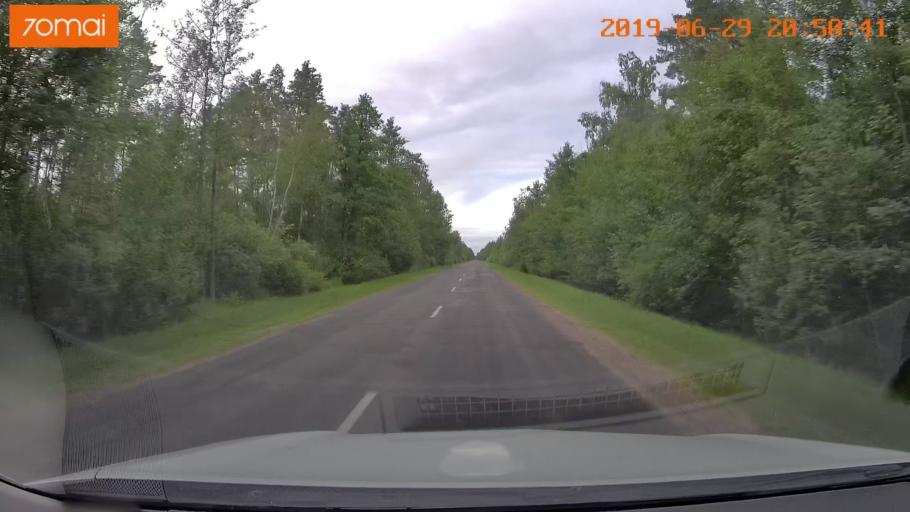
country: BY
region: Brest
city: Hantsavichy
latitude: 52.6794
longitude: 26.3393
